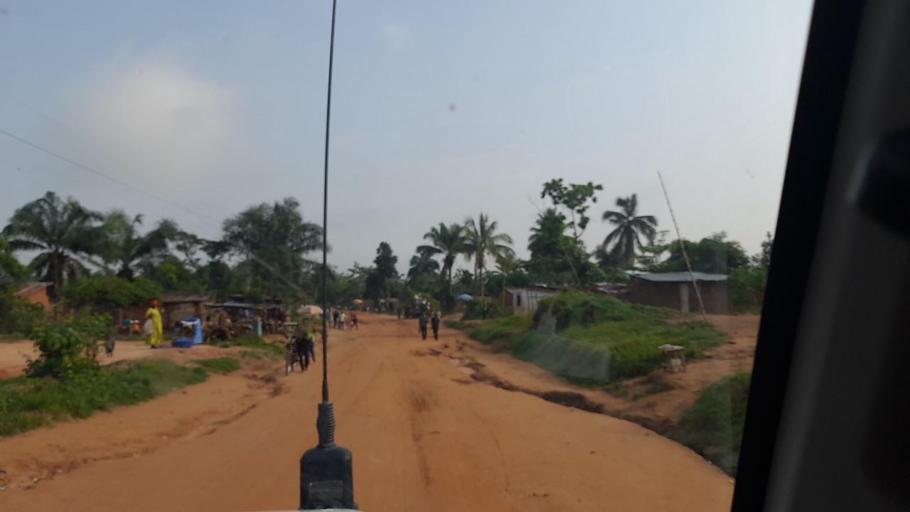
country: CD
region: Kasai-Occidental
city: Kananga
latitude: -5.8946
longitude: 22.3759
